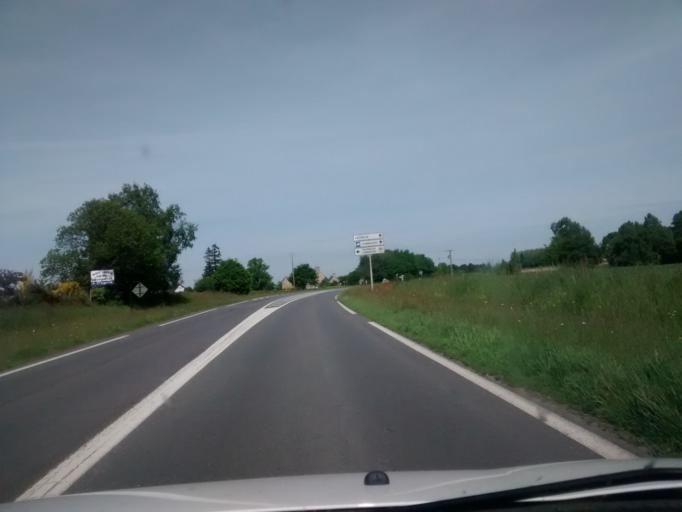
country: FR
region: Brittany
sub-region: Departement d'Ille-et-Vilaine
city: Tremblay
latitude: 48.4258
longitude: -1.4570
